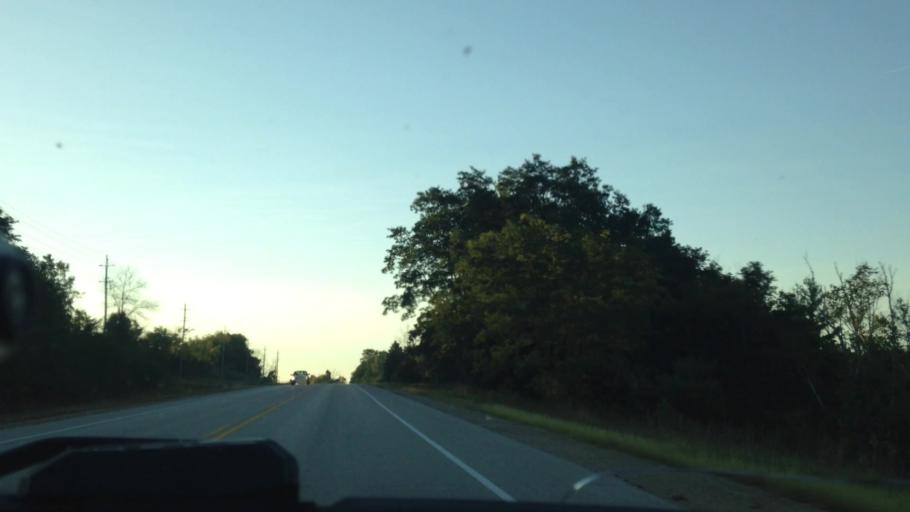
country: US
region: Wisconsin
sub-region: Ozaukee County
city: Saukville
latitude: 43.3946
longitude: -87.9768
